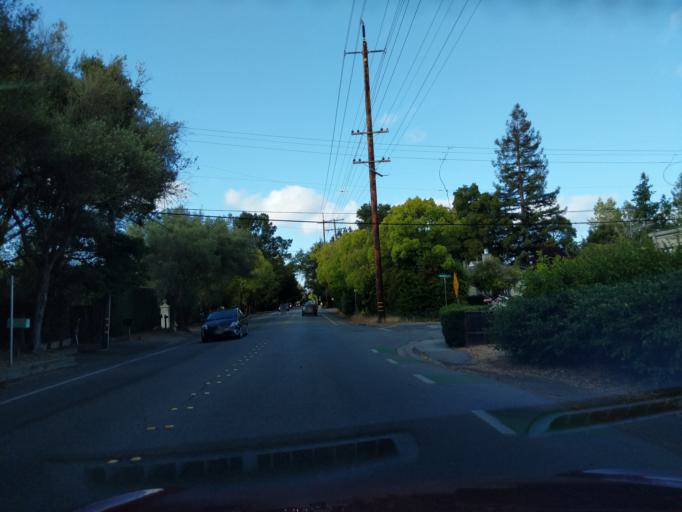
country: US
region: California
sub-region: San Mateo County
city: West Menlo Park
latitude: 37.4377
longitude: -122.2027
